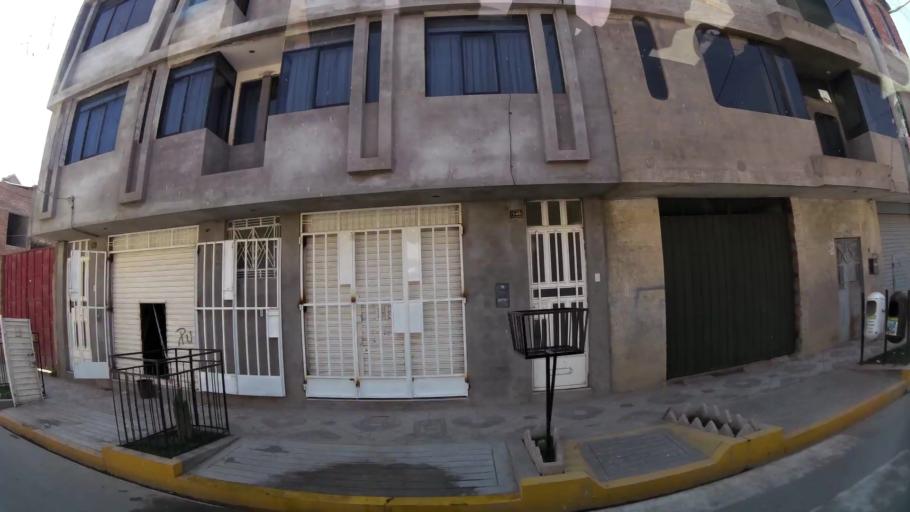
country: PE
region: Junin
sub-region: Provincia de Huancayo
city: El Tambo
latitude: -12.0752
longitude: -75.2294
